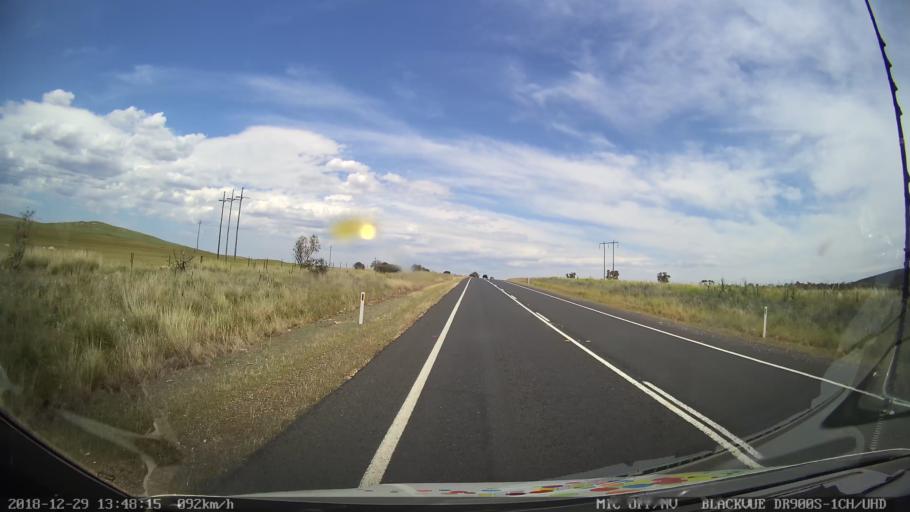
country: AU
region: New South Wales
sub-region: Cooma-Monaro
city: Cooma
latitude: -36.1378
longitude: 149.1468
